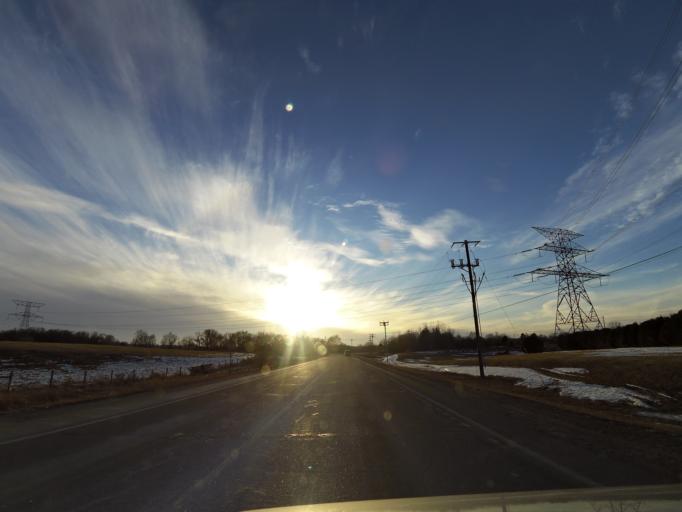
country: US
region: Minnesota
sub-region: Washington County
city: Lake Elmo
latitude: 44.9464
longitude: -92.8511
